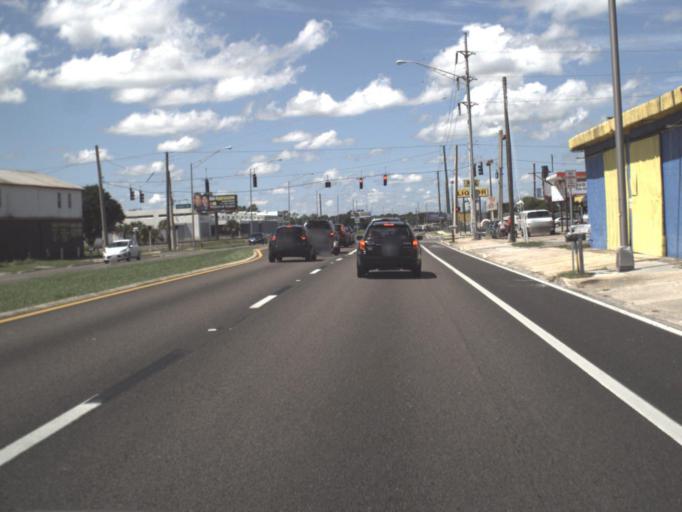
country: US
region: Florida
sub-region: Polk County
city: Crystal Lake
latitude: 28.0480
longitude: -81.9150
